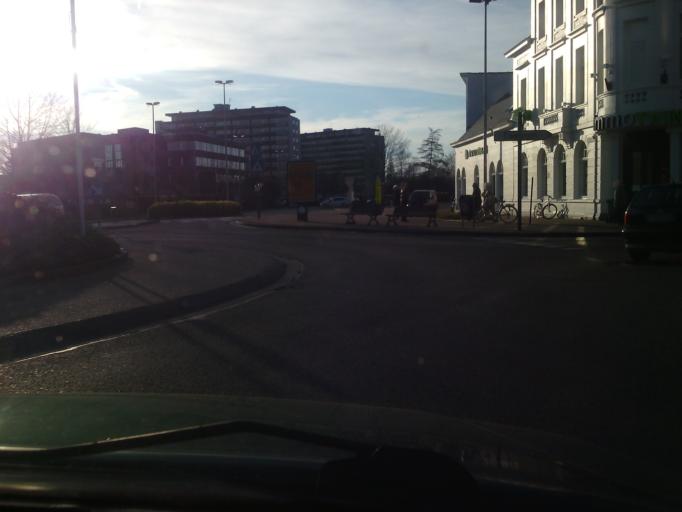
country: BE
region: Flanders
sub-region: Provincie Oost-Vlaanderen
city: Dendermonde
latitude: 51.0257
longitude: 4.1020
